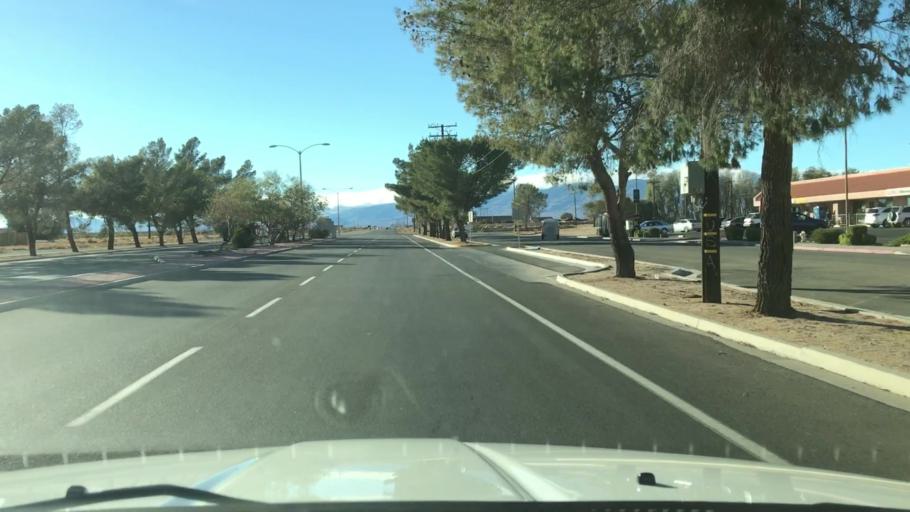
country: US
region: California
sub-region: Kern County
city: California City
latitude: 35.1258
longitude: -118.0013
